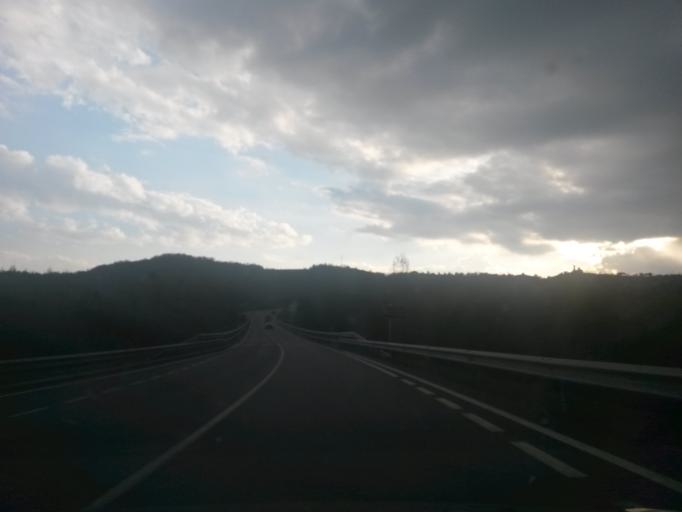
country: ES
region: Catalonia
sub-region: Provincia de Barcelona
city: Prats de Llucanes
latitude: 42.0086
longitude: 2.0546
